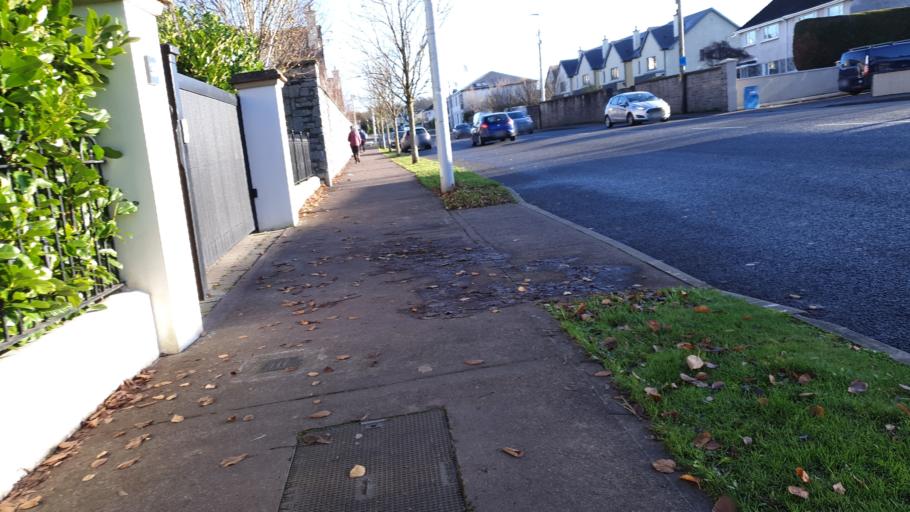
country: IE
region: Munster
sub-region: County Cork
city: Cork
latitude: 51.8912
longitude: -8.4451
